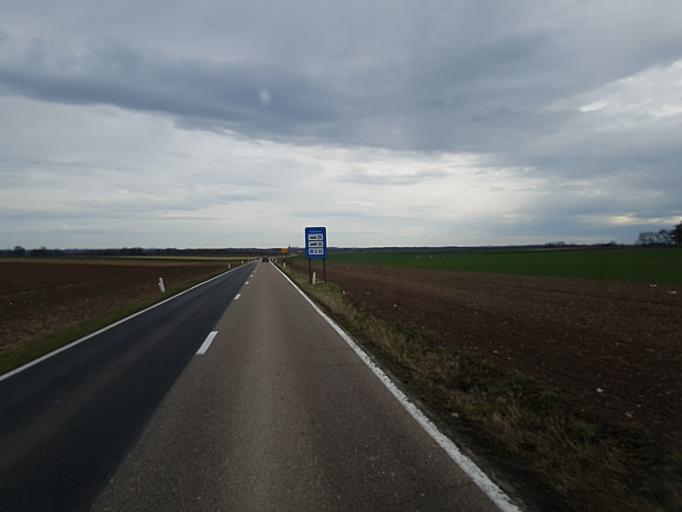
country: BE
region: Wallonia
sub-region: Province de Liege
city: Crisnee
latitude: 50.7433
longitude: 5.3786
